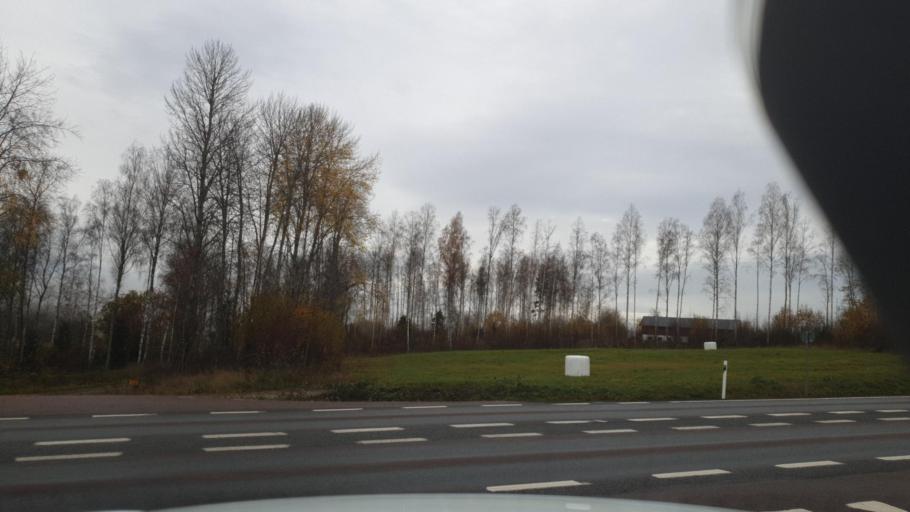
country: SE
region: Vaermland
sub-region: Arvika Kommun
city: Arvika
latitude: 59.6619
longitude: 12.7861
